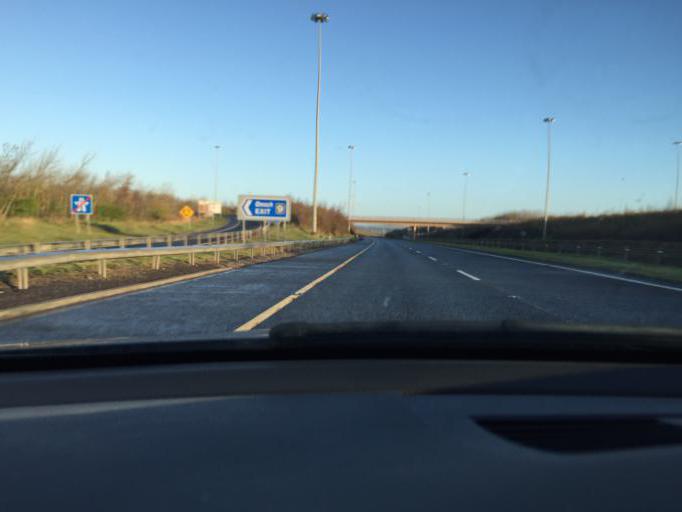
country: IE
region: Leinster
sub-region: Lu
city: Drogheda
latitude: 53.7005
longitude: -6.3811
